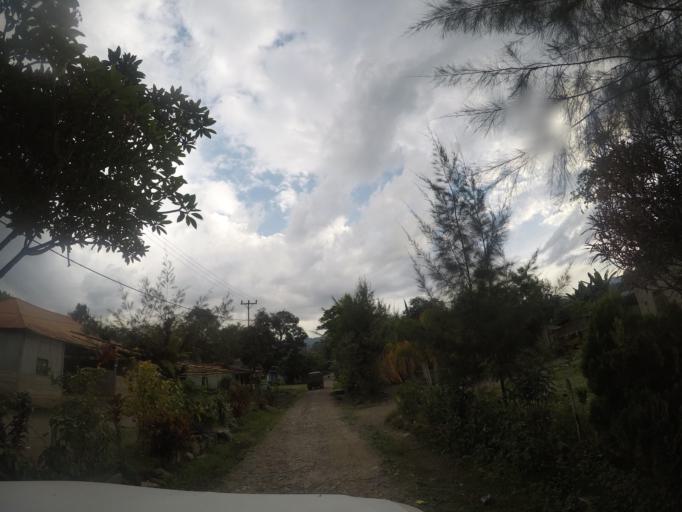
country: TL
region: Ermera
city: Gleno
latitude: -8.7277
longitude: 125.4458
